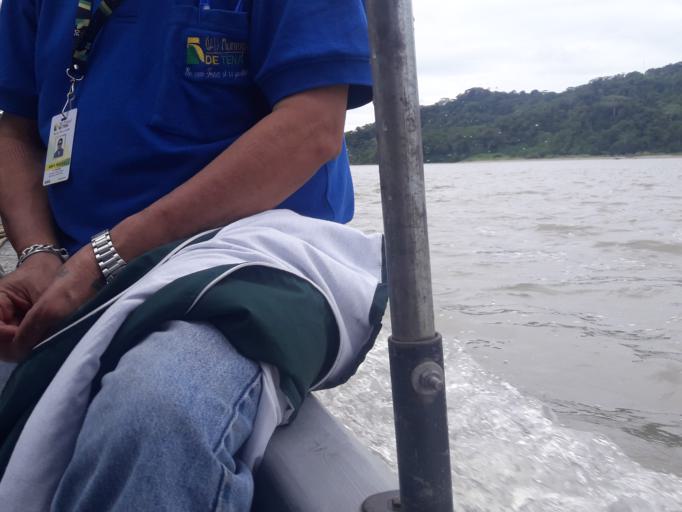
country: EC
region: Orellana
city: Boca Suno
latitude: -0.8774
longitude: -77.2755
